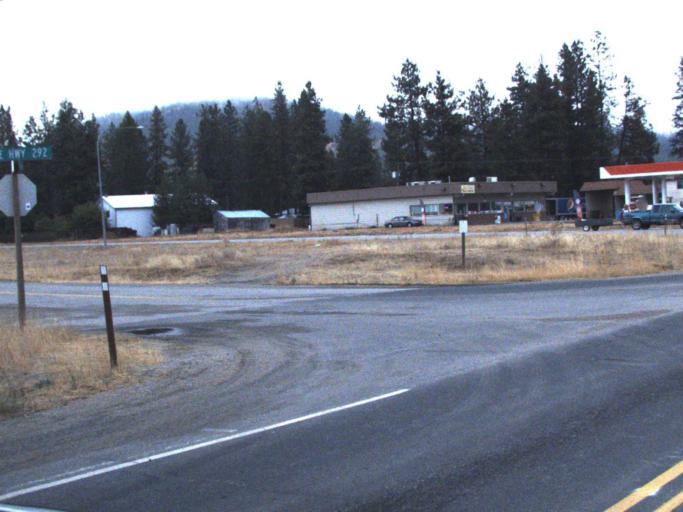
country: US
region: Washington
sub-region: Spokane County
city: Deer Park
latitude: 48.0596
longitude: -117.6216
